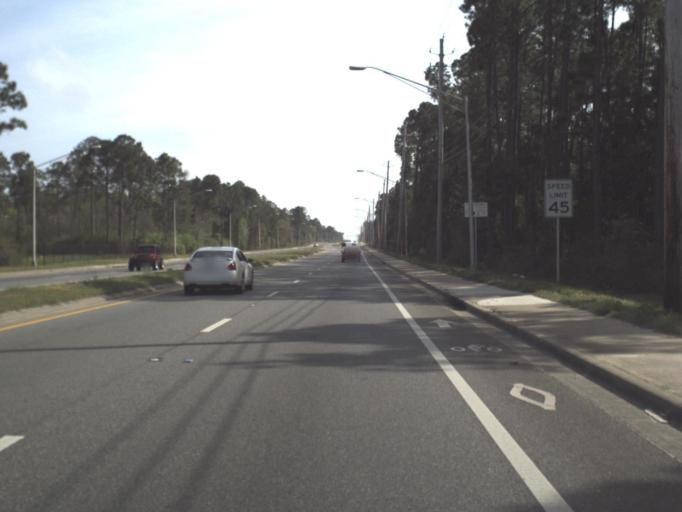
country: US
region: Florida
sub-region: Santa Rosa County
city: Navarre
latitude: 30.4304
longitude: -86.8665
